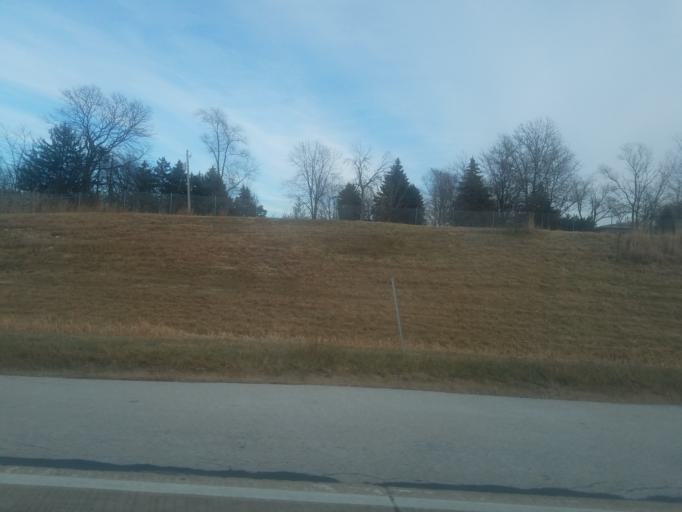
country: US
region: Illinois
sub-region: Cook County
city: Lemont
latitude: 41.6342
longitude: -88.0103
